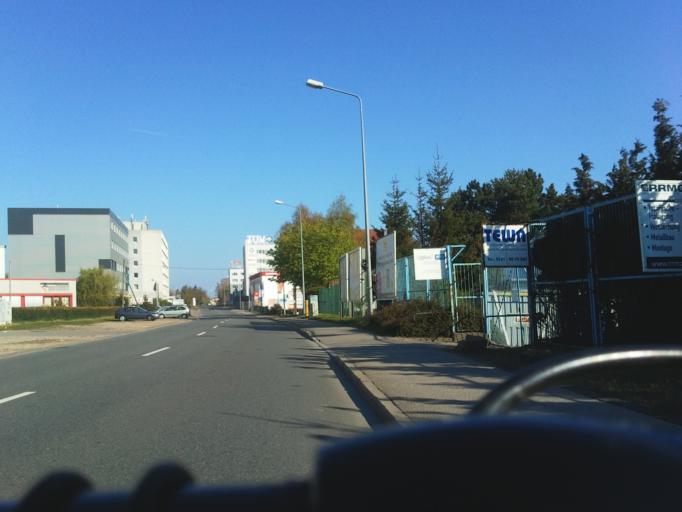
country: DE
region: Mecklenburg-Vorpommern
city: Rostock
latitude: 54.0973
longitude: 12.0979
